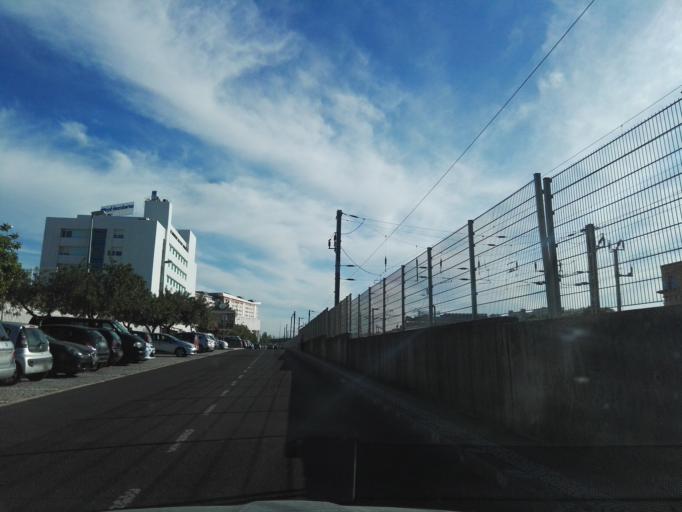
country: PT
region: Lisbon
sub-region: Loures
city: Moscavide
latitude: 38.7596
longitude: -9.0999
